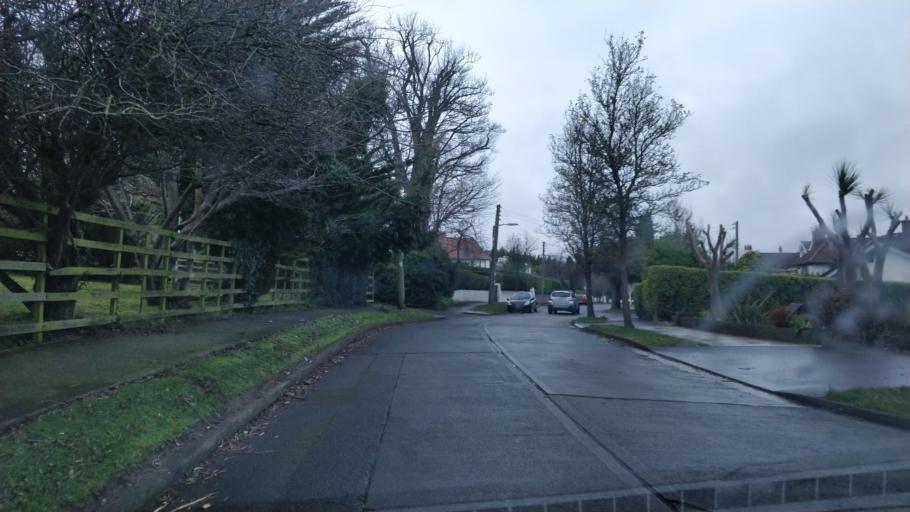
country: IE
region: Leinster
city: Foxrock
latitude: 53.2777
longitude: -6.1800
